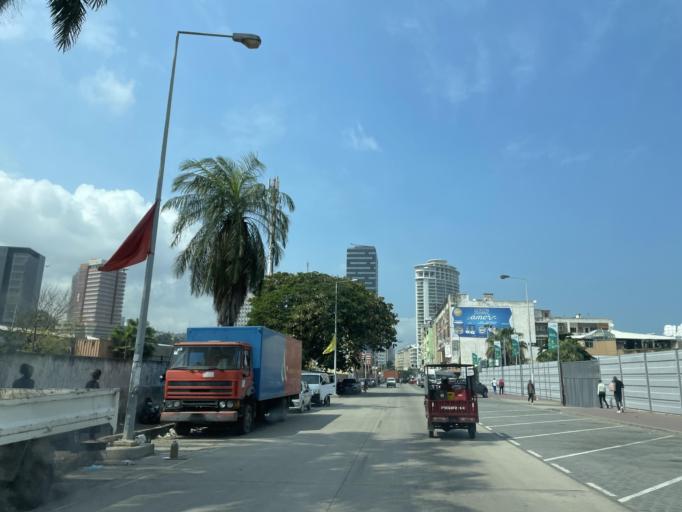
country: AO
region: Luanda
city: Luanda
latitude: -8.8060
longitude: 13.2428
